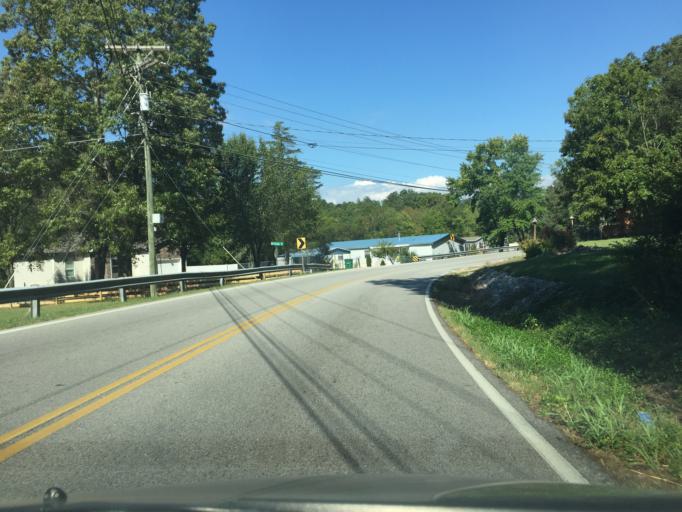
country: US
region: Tennessee
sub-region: Hamilton County
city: Harrison
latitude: 35.1082
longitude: -85.0832
